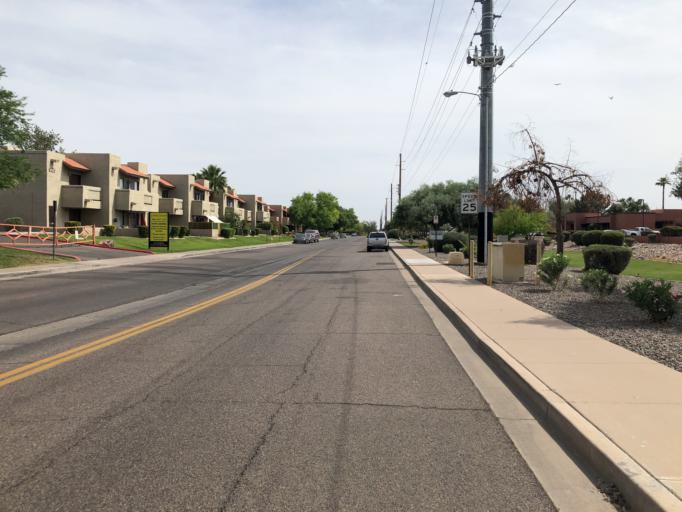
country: US
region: Arizona
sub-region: Maricopa County
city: Tempe
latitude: 33.4584
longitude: -111.9007
